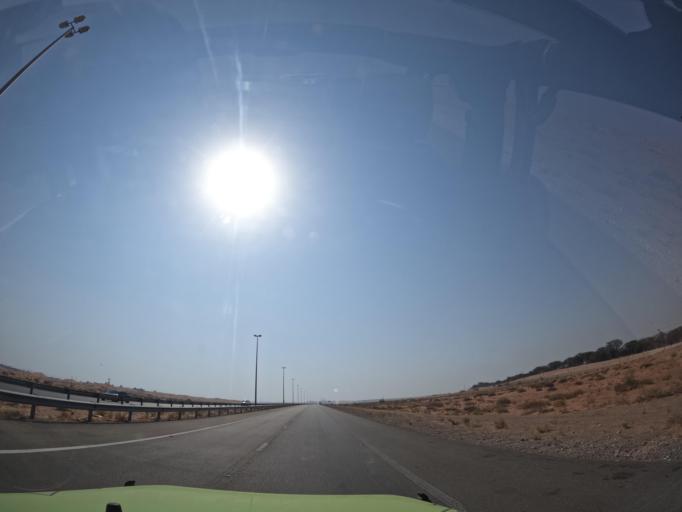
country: OM
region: Al Buraimi
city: Al Buraymi
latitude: 24.4006
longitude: 55.7141
